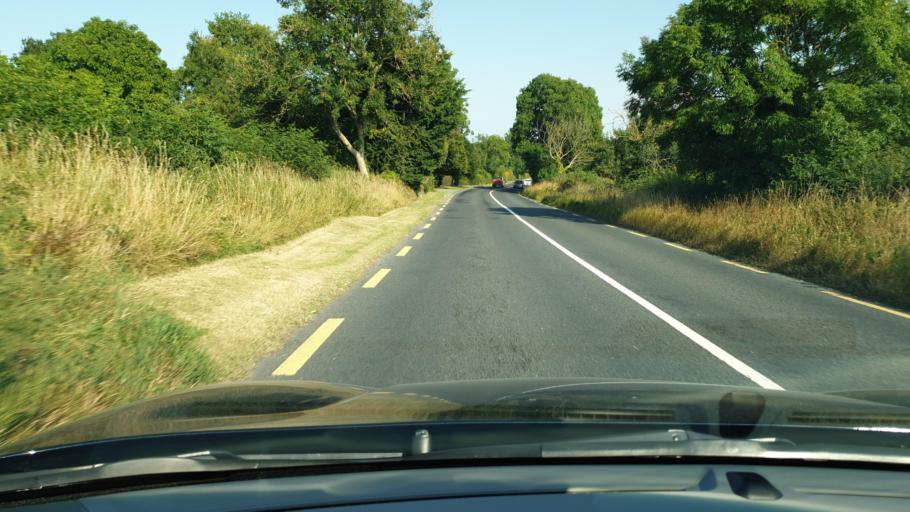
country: IE
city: Kentstown
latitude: 53.6339
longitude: -6.5714
